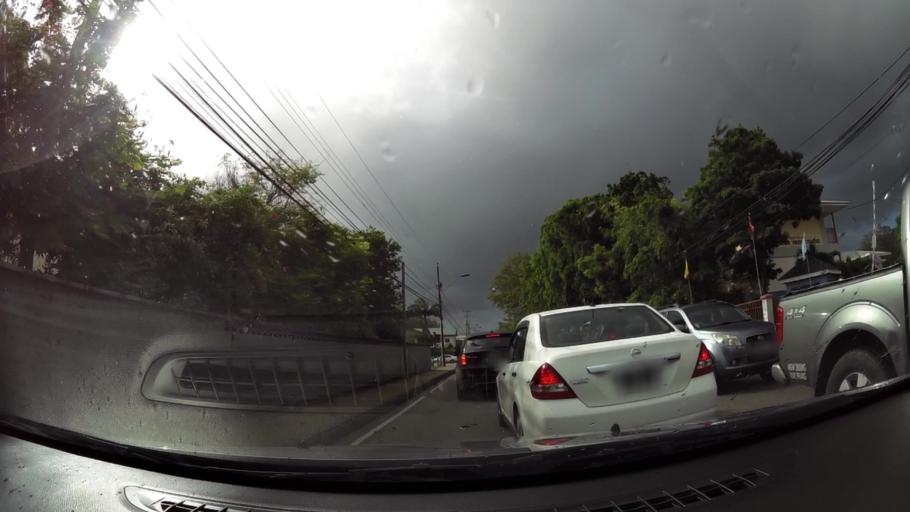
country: TT
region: Tunapuna/Piarco
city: Tunapuna
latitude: 10.6466
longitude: -61.4006
